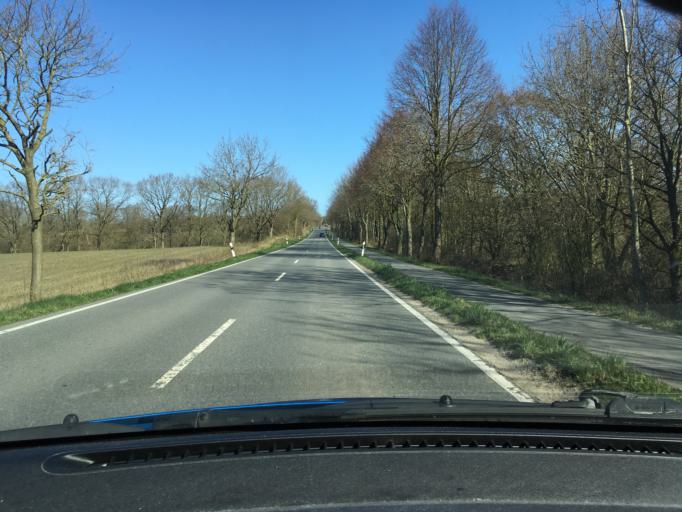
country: DE
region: Schleswig-Holstein
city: Kosel
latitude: 54.4950
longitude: 9.7479
